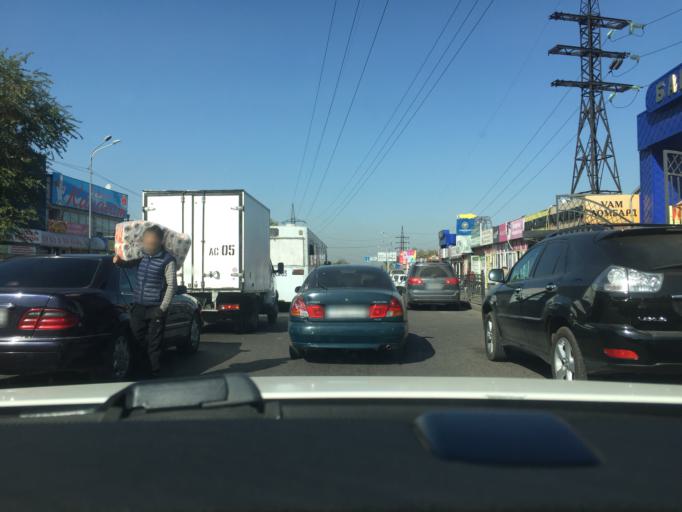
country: KZ
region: Almaty Qalasy
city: Almaty
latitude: 43.2565
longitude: 76.8873
